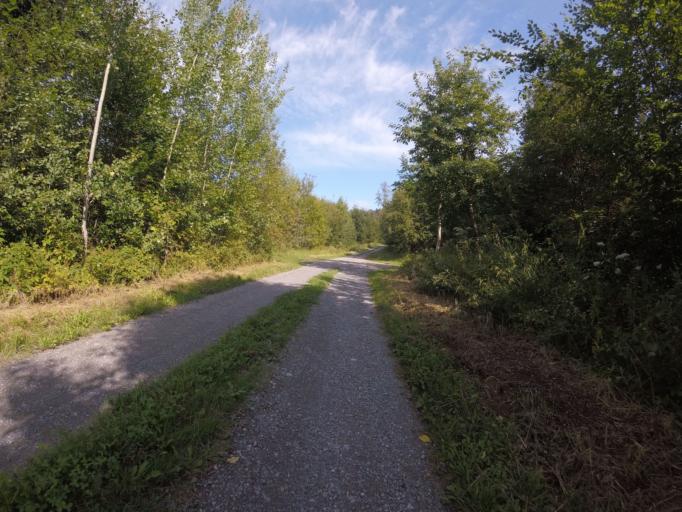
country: DE
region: Baden-Wuerttemberg
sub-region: Regierungsbezirk Stuttgart
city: Sulzbach an der Murr
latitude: 48.9722
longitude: 9.5176
